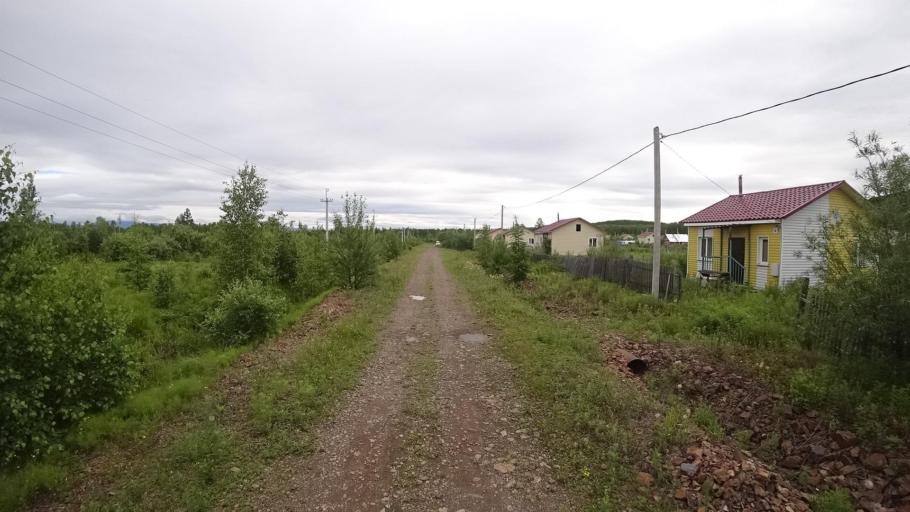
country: RU
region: Khabarovsk Krai
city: Amursk
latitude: 49.8958
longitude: 136.1607
